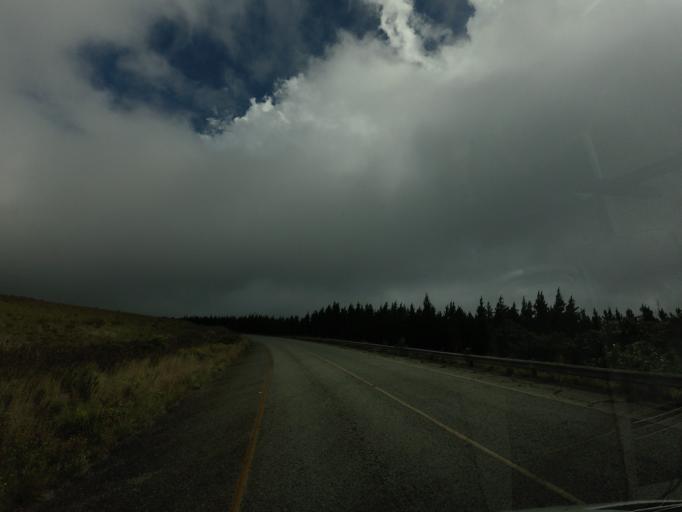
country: ZA
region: Mpumalanga
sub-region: Ehlanzeni District
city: Graksop
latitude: -24.8602
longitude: 30.8902
